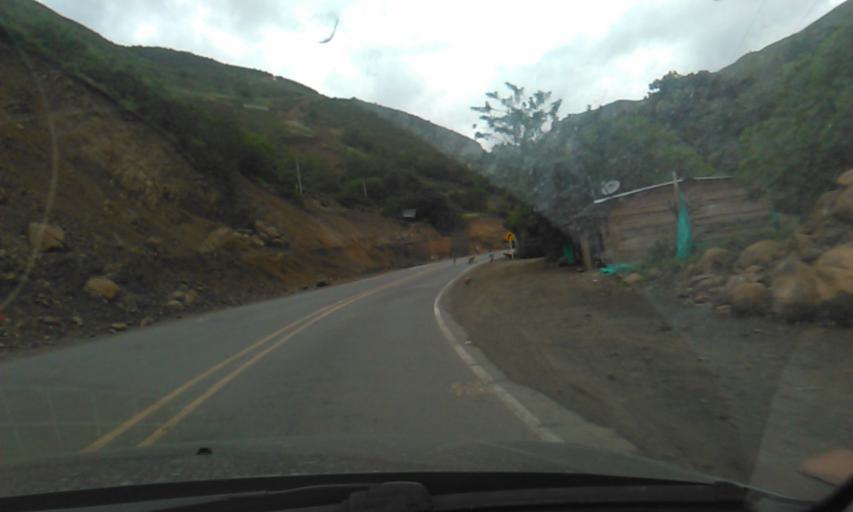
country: CO
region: Valle del Cauca
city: Restrepo
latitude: 3.7880
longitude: -76.6428
